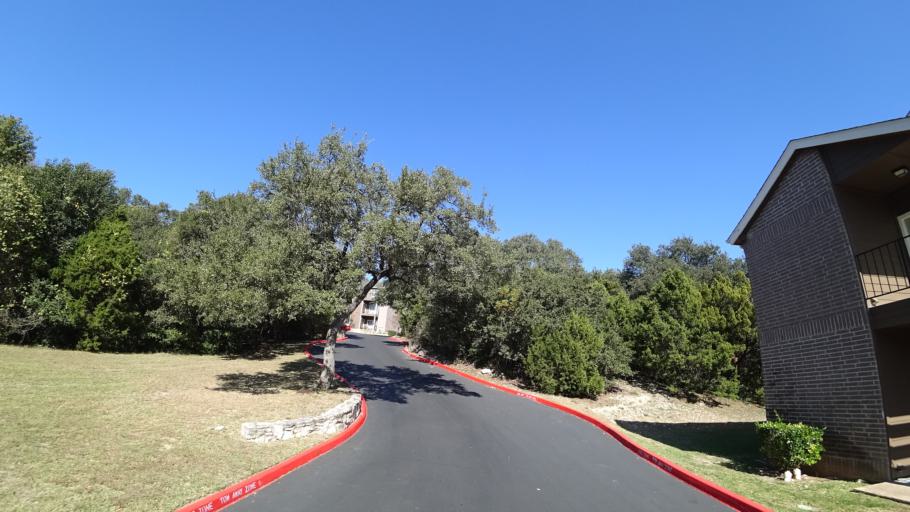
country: US
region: Texas
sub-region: Williamson County
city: Jollyville
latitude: 30.4115
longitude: -97.7511
